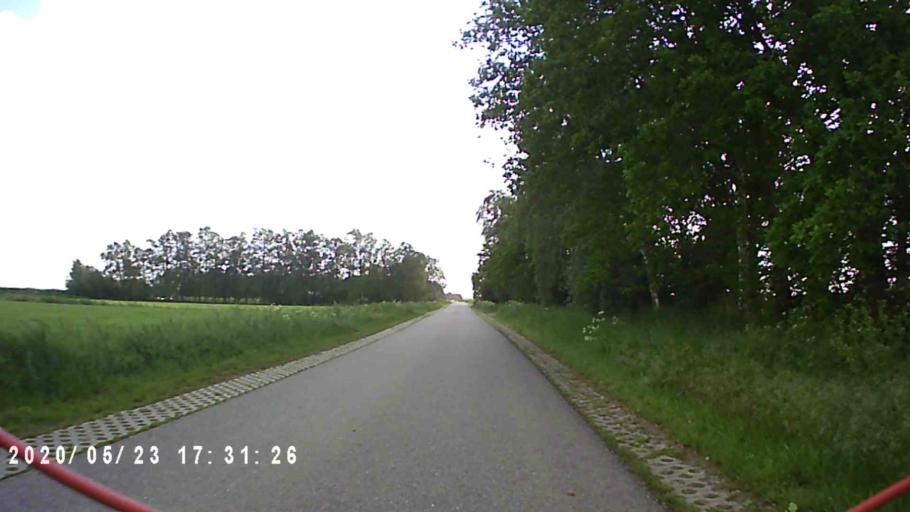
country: NL
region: Groningen
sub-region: Gemeente Slochteren
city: Slochteren
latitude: 53.2571
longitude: 6.7708
